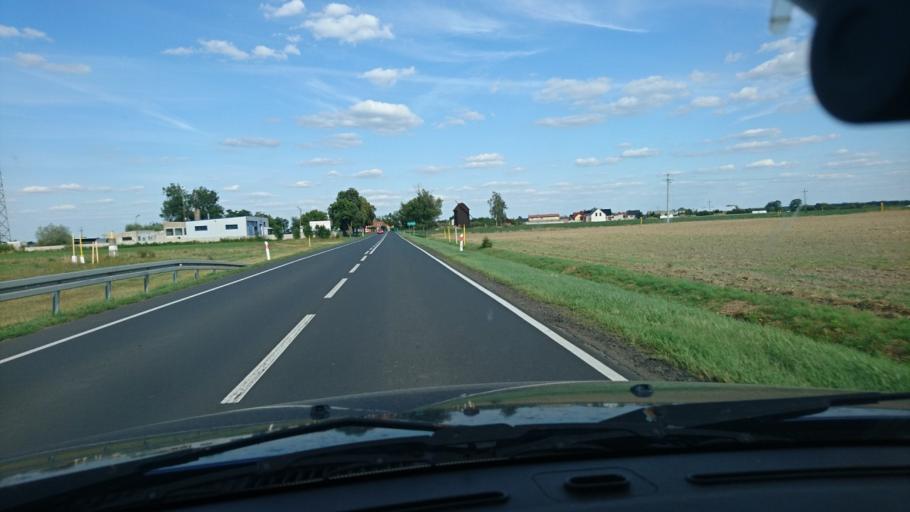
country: PL
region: Greater Poland Voivodeship
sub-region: Powiat krotoszynski
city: Kobylin
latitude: 51.7103
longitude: 17.2080
